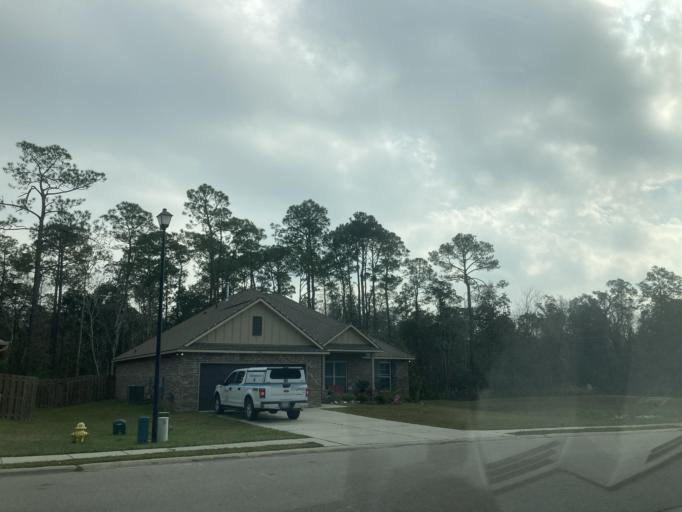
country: US
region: Mississippi
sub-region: Harrison County
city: Long Beach
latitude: 30.3699
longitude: -89.1581
